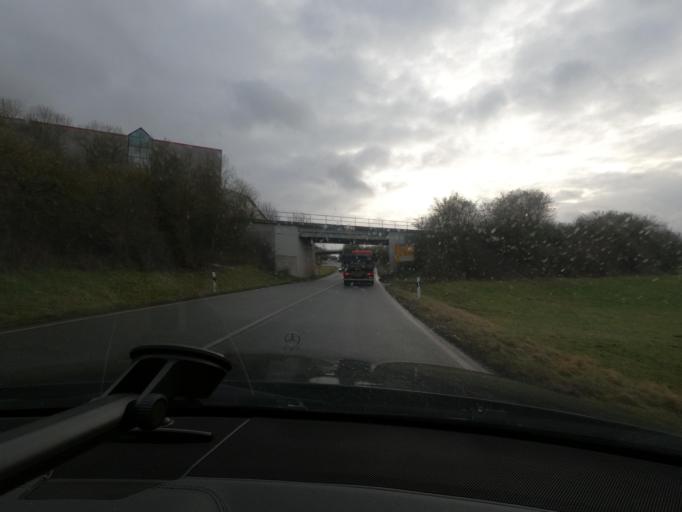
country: DE
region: Hesse
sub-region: Regierungsbezirk Kassel
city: Wolfhagen
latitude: 51.3347
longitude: 9.1665
